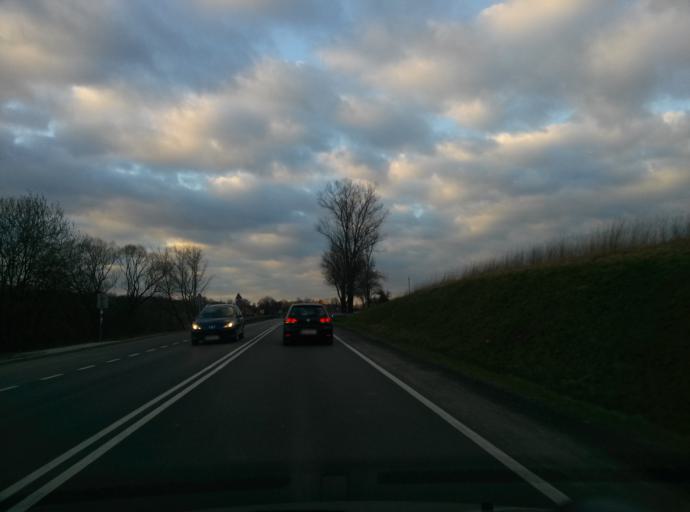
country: PL
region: Lesser Poland Voivodeship
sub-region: Powiat brzeski
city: Okocim
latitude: 49.9469
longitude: 20.5862
